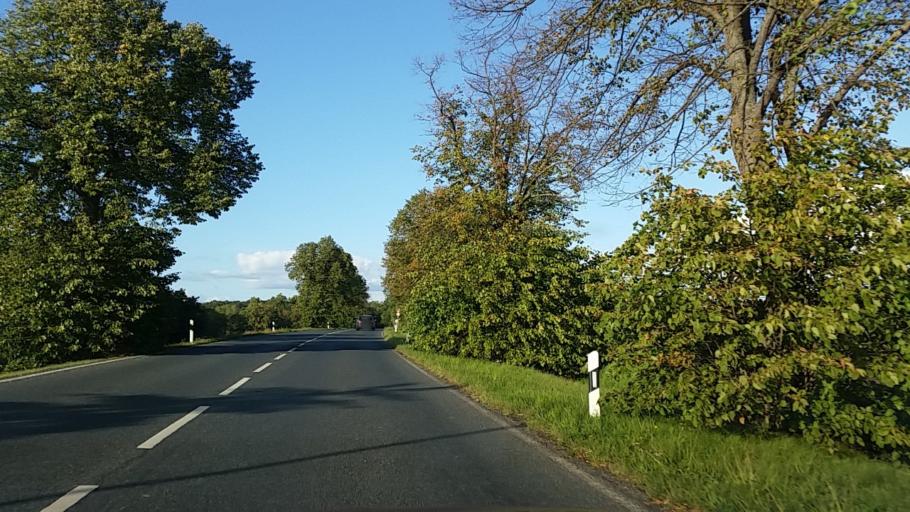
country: DE
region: Lower Saxony
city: Vordorf
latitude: 52.3349
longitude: 10.5215
